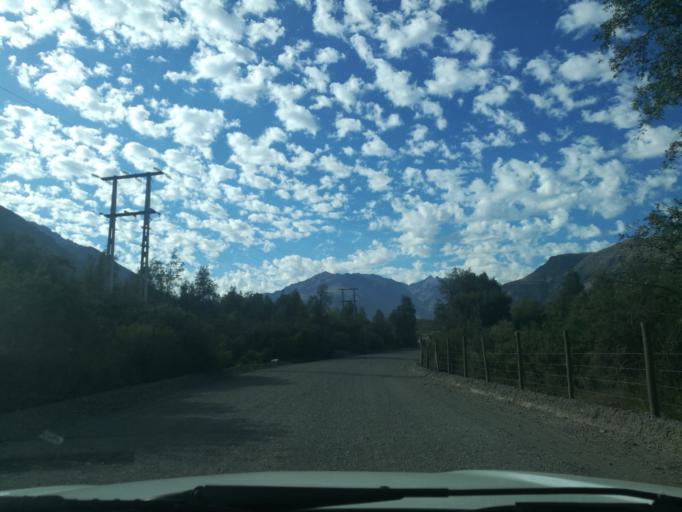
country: CL
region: O'Higgins
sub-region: Provincia de Cachapoal
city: Machali
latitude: -34.2889
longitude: -70.4370
